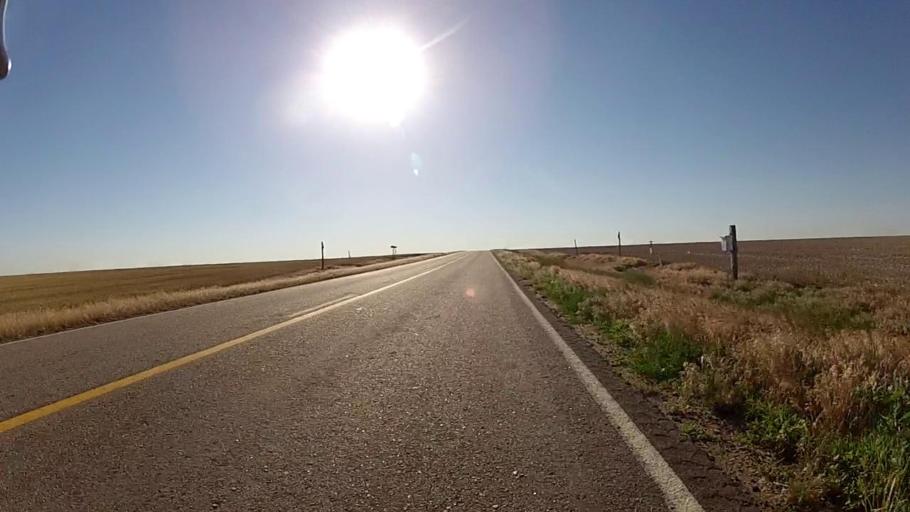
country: US
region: Kansas
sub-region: Ford County
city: Dodge City
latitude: 37.6462
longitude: -99.8319
